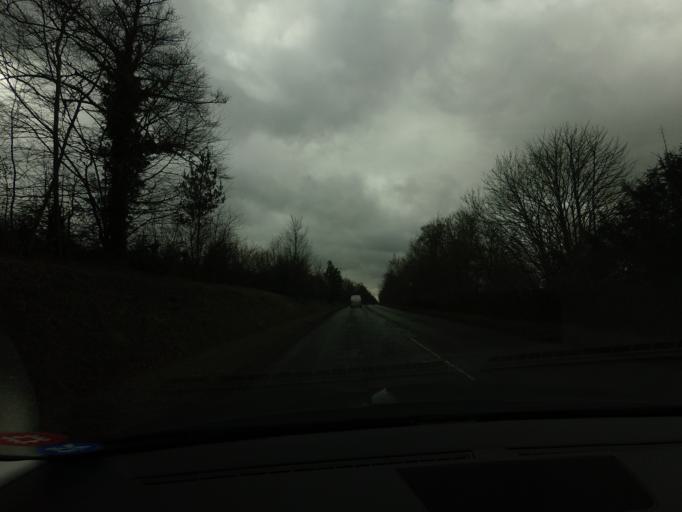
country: GB
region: England
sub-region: Kent
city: Eynsford
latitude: 51.3542
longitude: 0.1994
